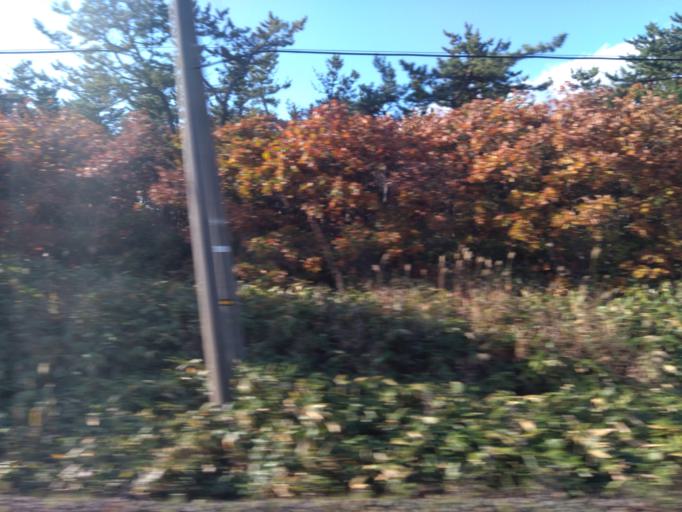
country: JP
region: Hokkaido
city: Niseko Town
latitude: 42.5638
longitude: 140.4336
